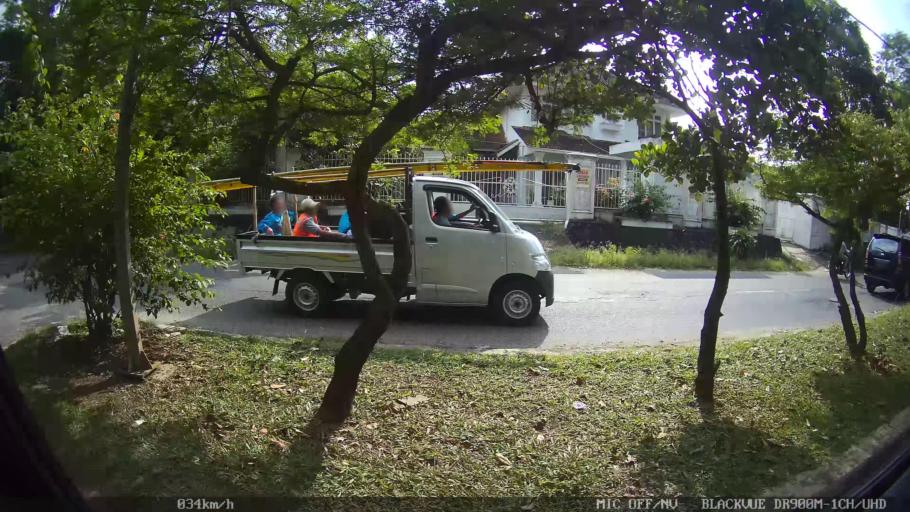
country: ID
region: Lampung
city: Bandarlampung
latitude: -5.4300
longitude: 105.2461
